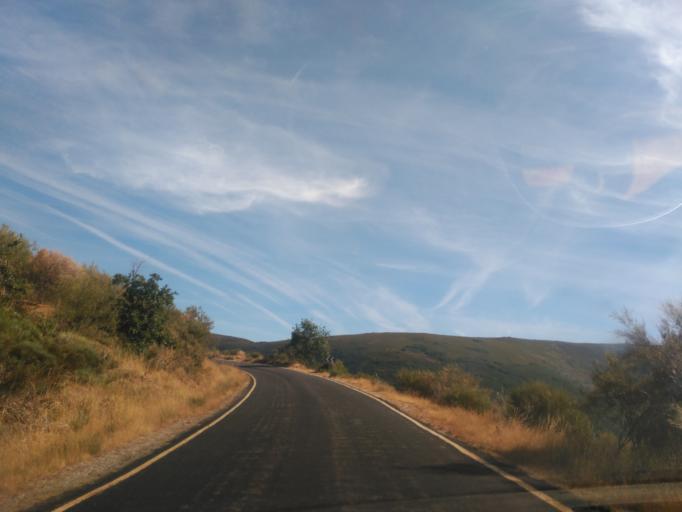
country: ES
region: Castille and Leon
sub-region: Provincia de Zamora
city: Trefacio
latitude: 42.1448
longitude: -6.7161
